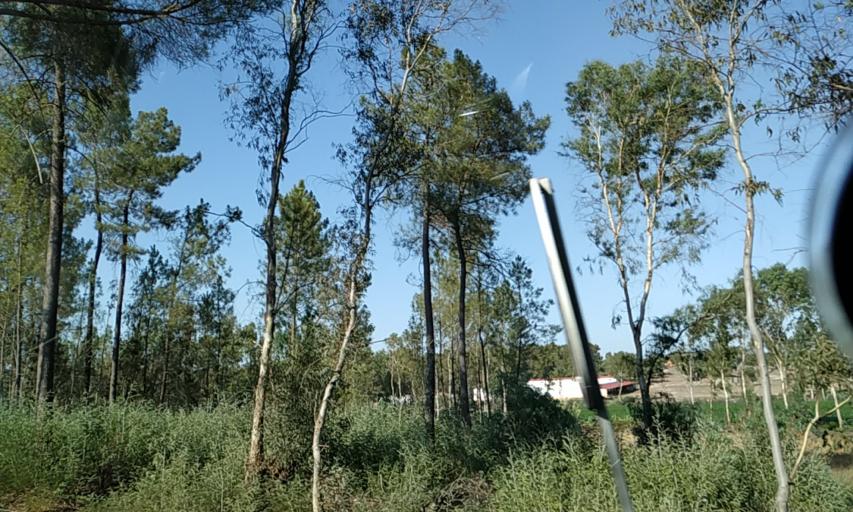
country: PT
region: Santarem
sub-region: Coruche
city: Coruche
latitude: 38.9999
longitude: -8.5574
